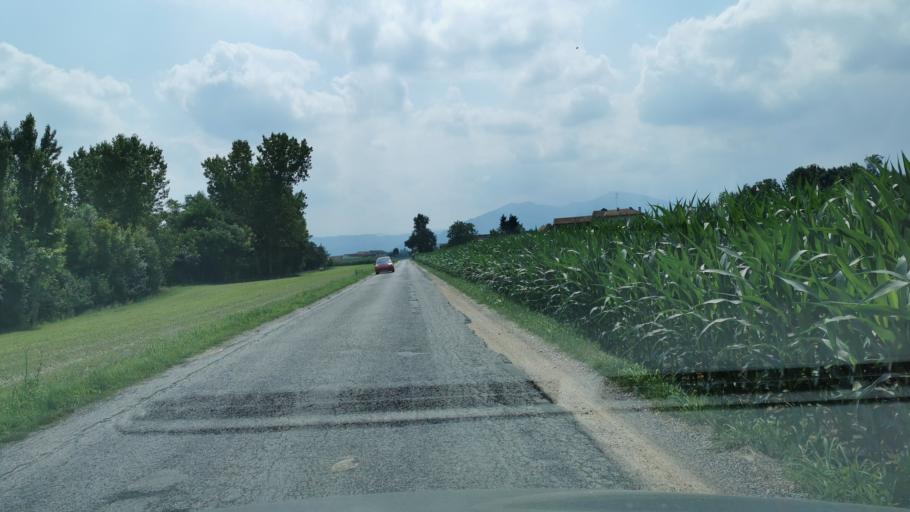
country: IT
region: Piedmont
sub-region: Provincia di Cuneo
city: Roata Rossi
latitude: 44.4343
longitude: 7.4929
